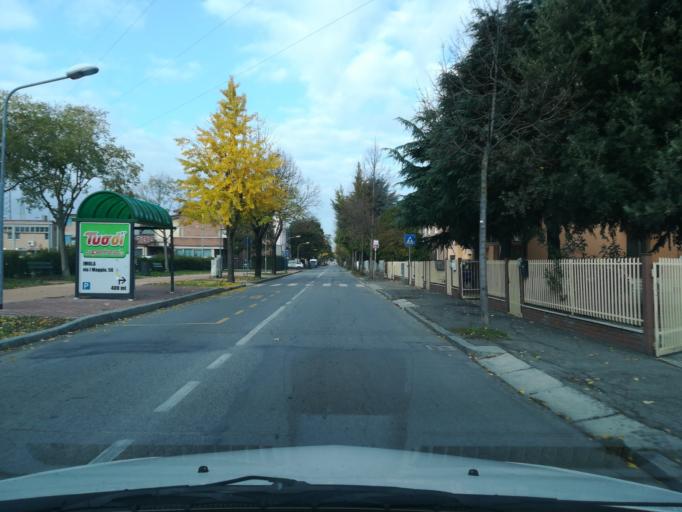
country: IT
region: Emilia-Romagna
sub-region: Provincia di Bologna
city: Imola
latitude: 44.3622
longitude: 11.7204
